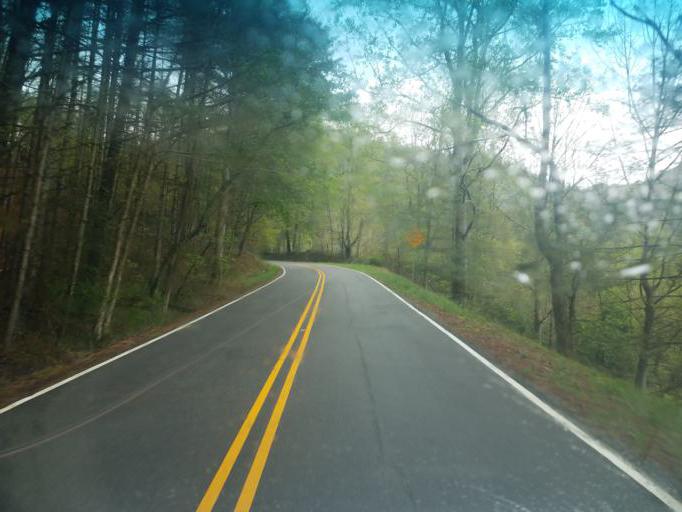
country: US
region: Virginia
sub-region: Washington County
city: Glade Spring
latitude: 36.6368
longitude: -81.7489
